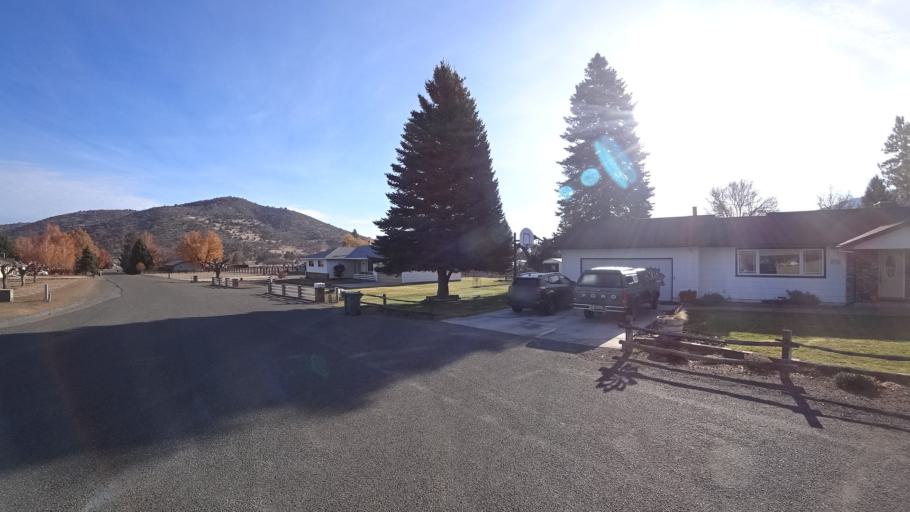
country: US
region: California
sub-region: Siskiyou County
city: Yreka
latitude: 41.6799
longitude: -122.6387
